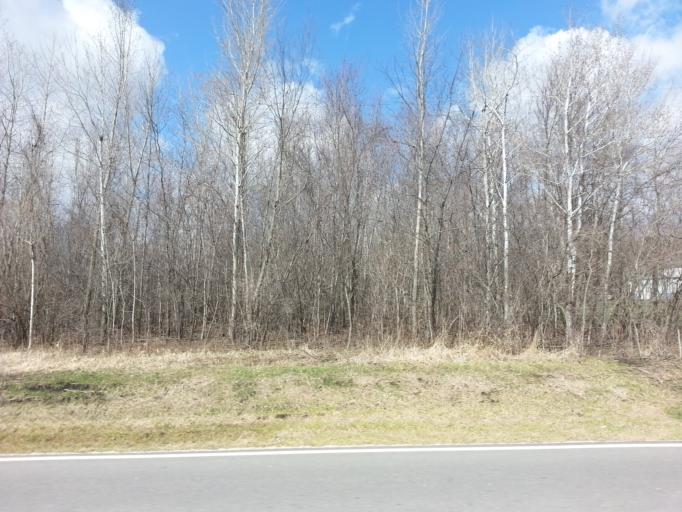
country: US
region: Minnesota
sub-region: Dodge County
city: Dodge Center
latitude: 44.0806
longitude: -92.8235
